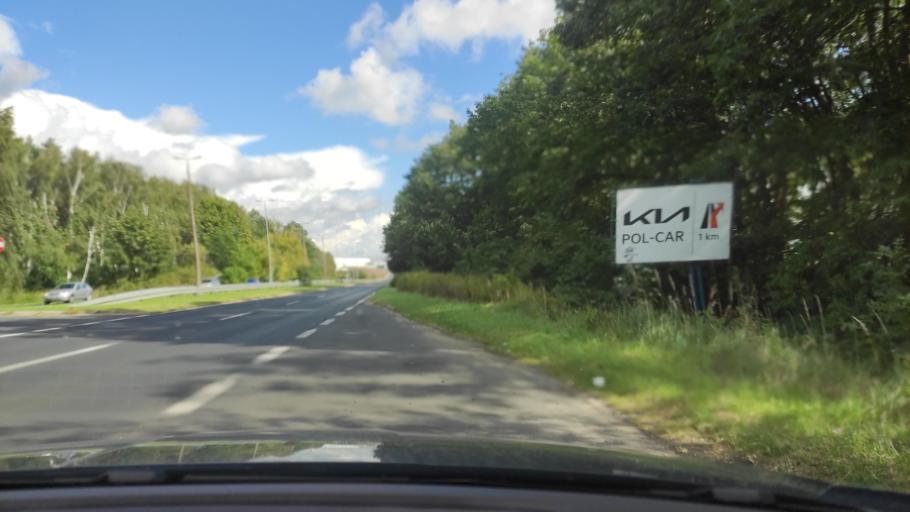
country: PL
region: Greater Poland Voivodeship
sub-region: Powiat poznanski
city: Czerwonak
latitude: 52.4105
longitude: 17.0103
